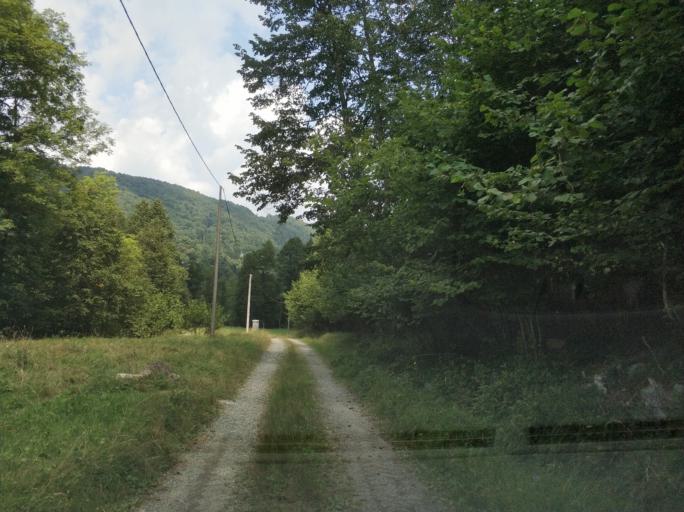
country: IT
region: Piedmont
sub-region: Provincia di Torino
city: Viu
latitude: 45.2097
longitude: 7.3939
